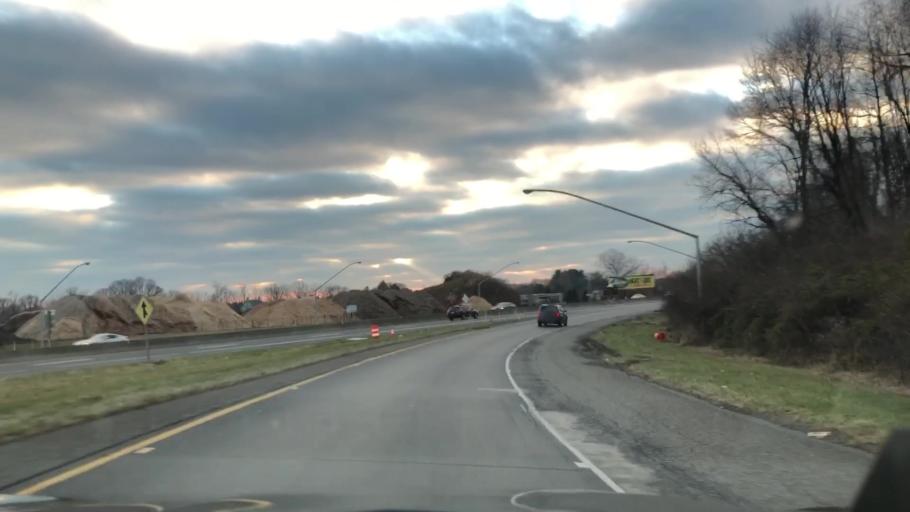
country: US
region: Pennsylvania
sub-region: Northampton County
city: Palmer Heights
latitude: 40.6836
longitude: -75.2938
